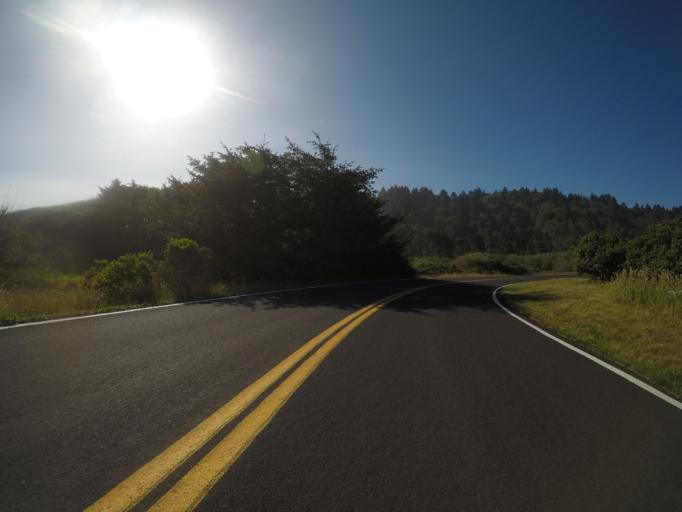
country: US
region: California
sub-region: Humboldt County
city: Westhaven-Moonstone
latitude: 41.2866
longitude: -124.0898
